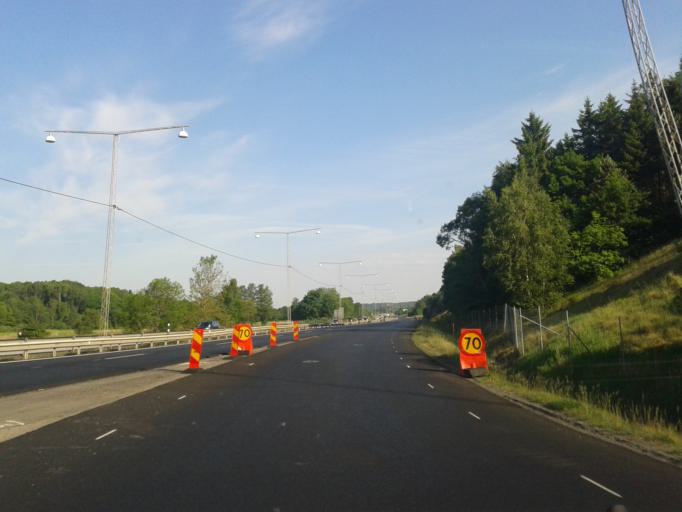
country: SE
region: Vaestra Goetaland
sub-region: Kungalvs Kommun
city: Kungalv
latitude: 57.8863
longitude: 11.9435
